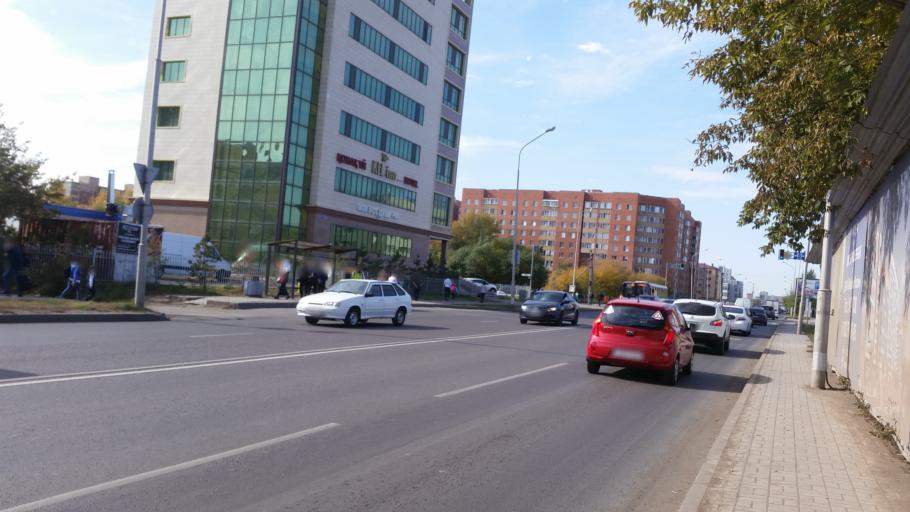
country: KZ
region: Astana Qalasy
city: Astana
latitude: 51.1591
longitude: 71.4923
